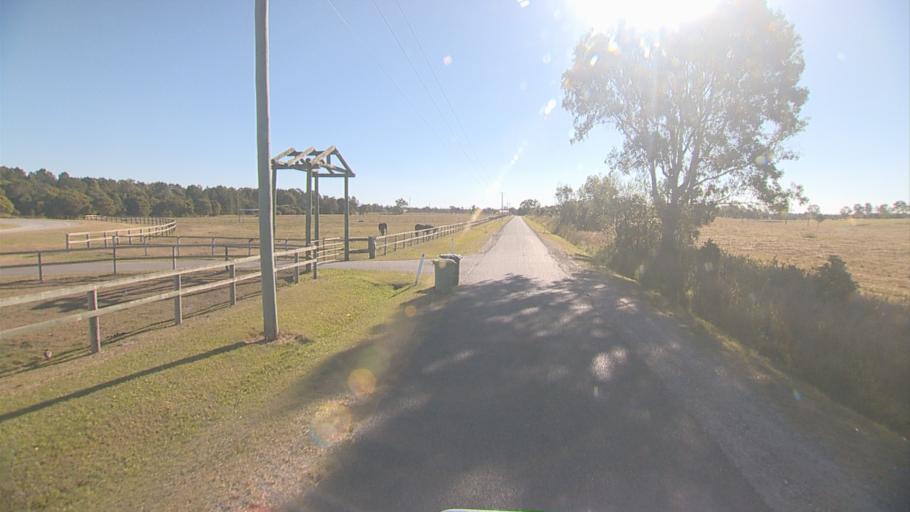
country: AU
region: Queensland
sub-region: Logan
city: Chambers Flat
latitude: -27.7687
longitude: 153.0657
